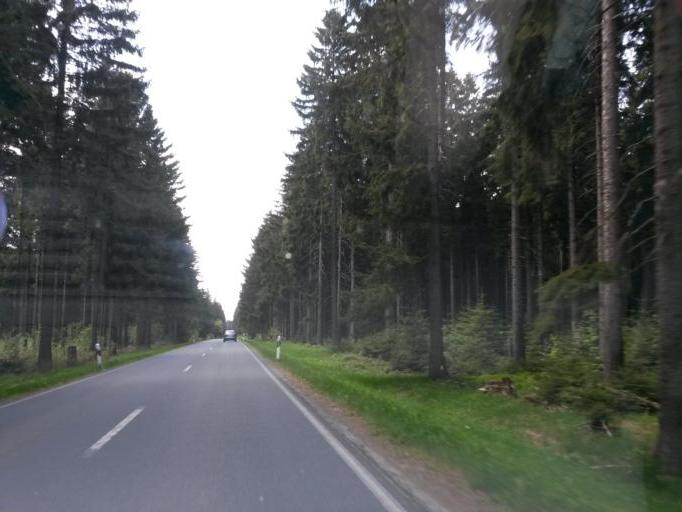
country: DE
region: Saxony
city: Pohl
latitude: 50.3880
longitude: 12.3673
